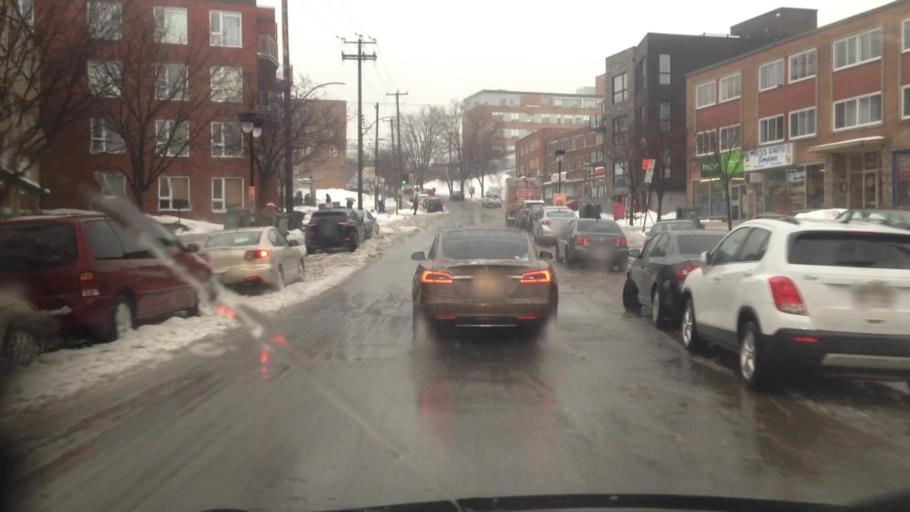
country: CA
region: Quebec
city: Mont-Royal
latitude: 45.5098
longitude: -73.6305
